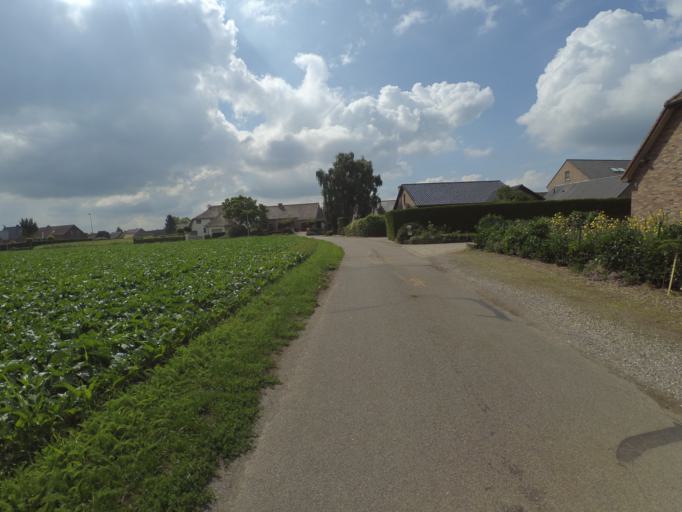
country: BE
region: Flanders
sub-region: Provincie Limburg
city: Maaseik
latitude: 51.1057
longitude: 5.7733
